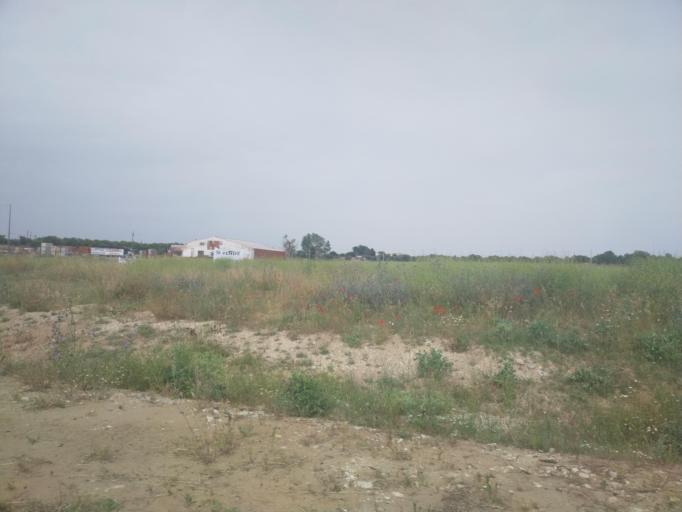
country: ES
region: Castille-La Mancha
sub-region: Province of Toledo
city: Polan
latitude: 39.7840
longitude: -4.1595
